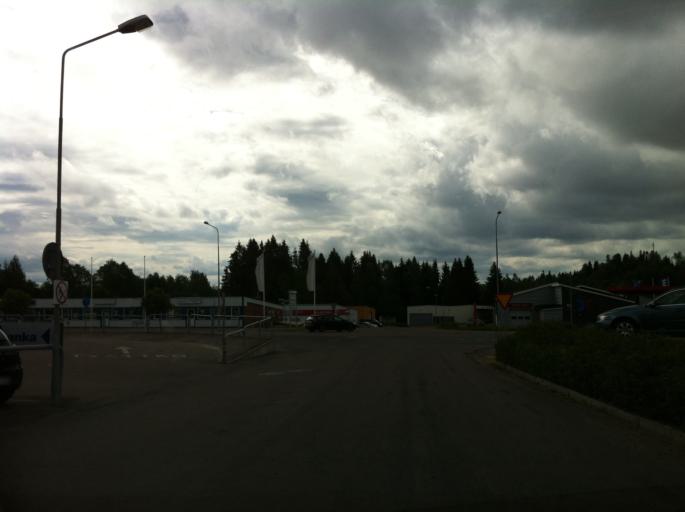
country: SE
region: Vaermland
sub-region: Sunne Kommun
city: Sunne
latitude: 59.8383
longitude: 13.1280
